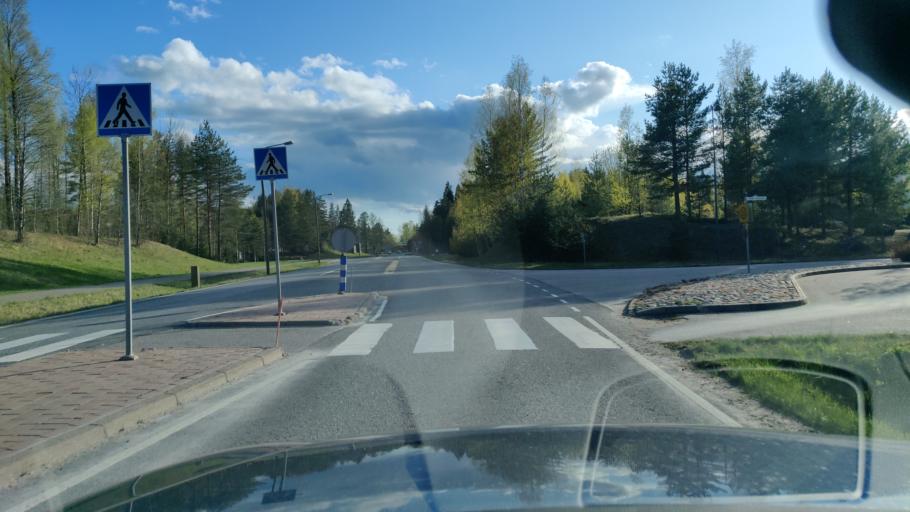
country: FI
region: Uusimaa
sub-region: Helsinki
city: Tuusula
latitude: 60.4168
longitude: 25.0073
